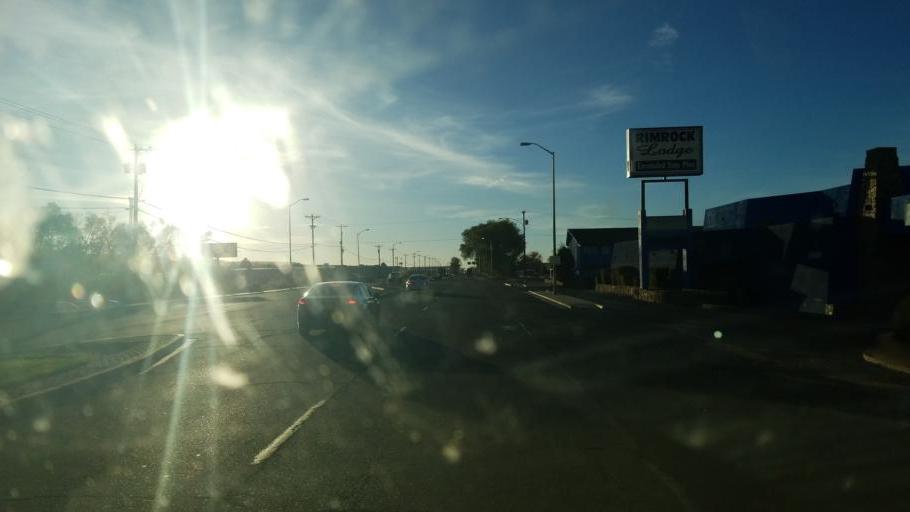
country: US
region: New Mexico
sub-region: San Juan County
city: Farmington
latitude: 36.7194
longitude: -108.1744
